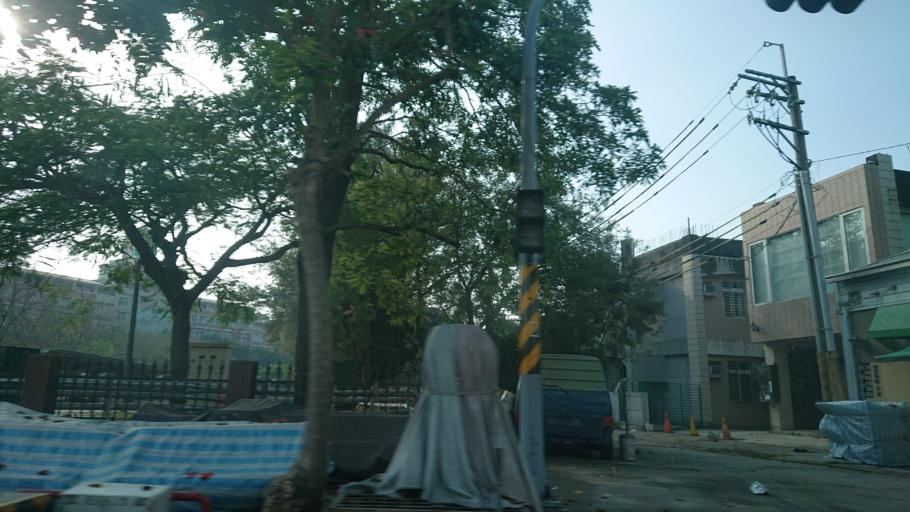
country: TW
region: Taiwan
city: Xinying
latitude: 23.1936
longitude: 120.2712
